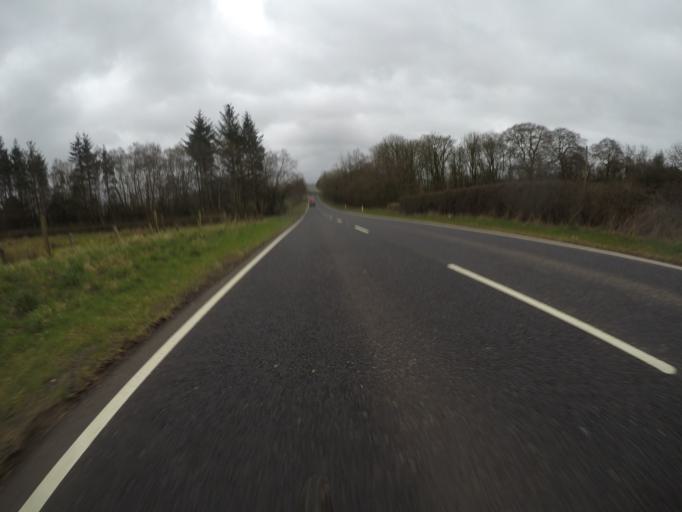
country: GB
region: Scotland
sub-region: East Ayrshire
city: Galston
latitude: 55.6158
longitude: -4.3818
